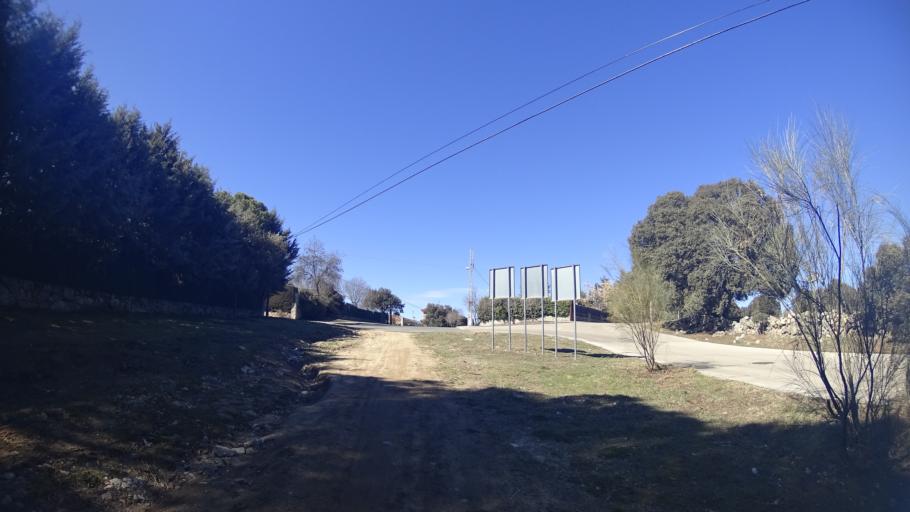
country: ES
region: Madrid
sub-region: Provincia de Madrid
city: Colmenarejo
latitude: 40.5498
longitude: -4.0023
